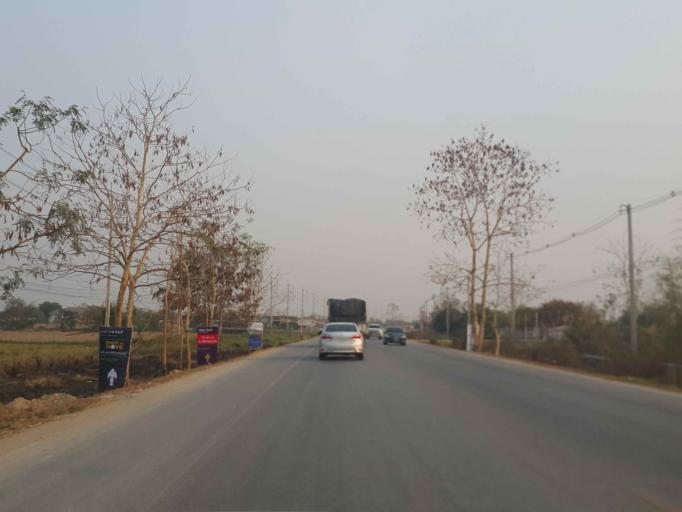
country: TH
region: Chiang Mai
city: San Sai
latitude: 18.7937
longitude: 99.0673
